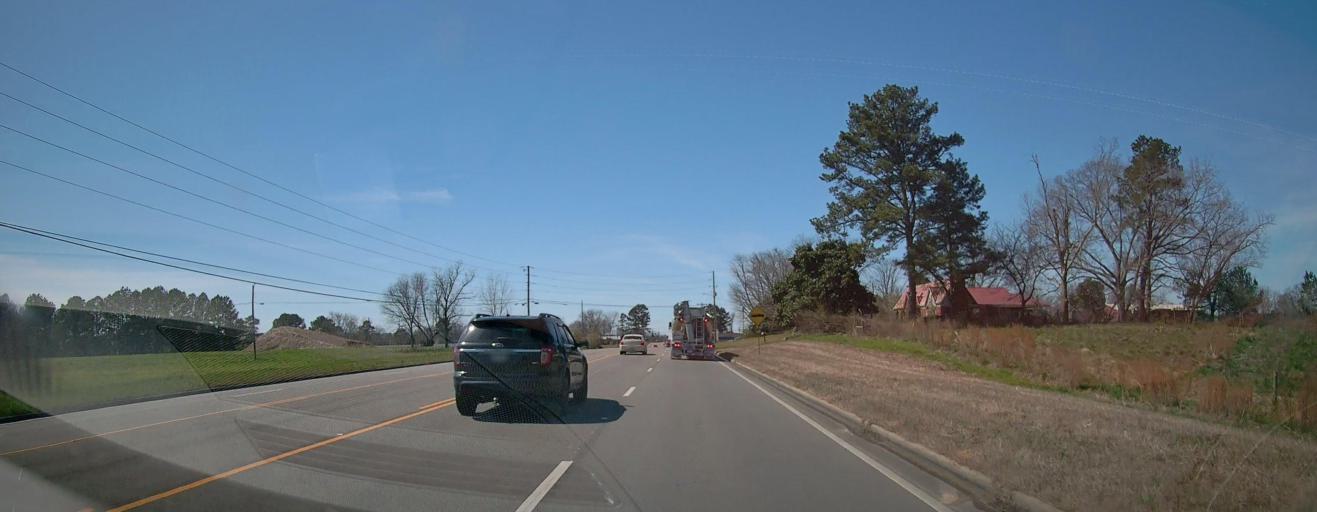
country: US
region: Alabama
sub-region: Cullman County
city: Cullman
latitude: 34.1782
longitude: -86.7396
